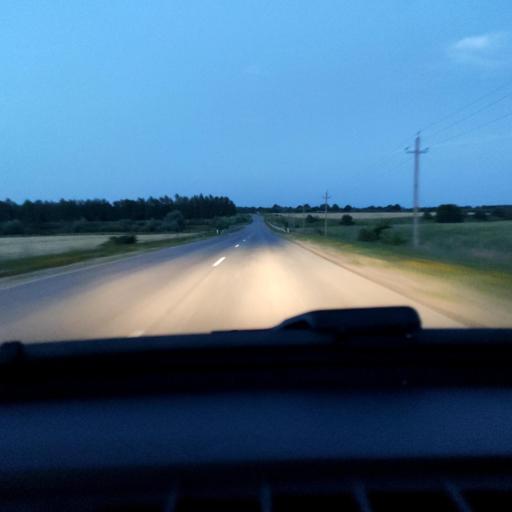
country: RU
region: Lipetsk
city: Zadonsk
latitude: 52.2965
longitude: 38.8320
